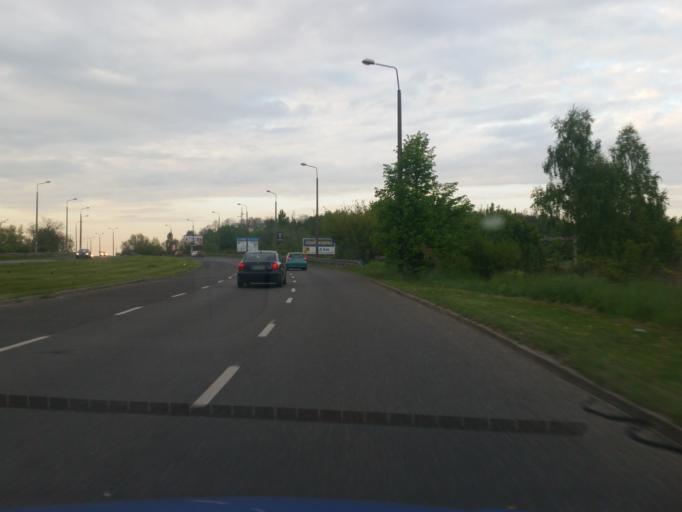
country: PL
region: Silesian Voivodeship
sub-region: Powiat bedzinski
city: Bedzin
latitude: 50.2960
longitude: 19.1710
